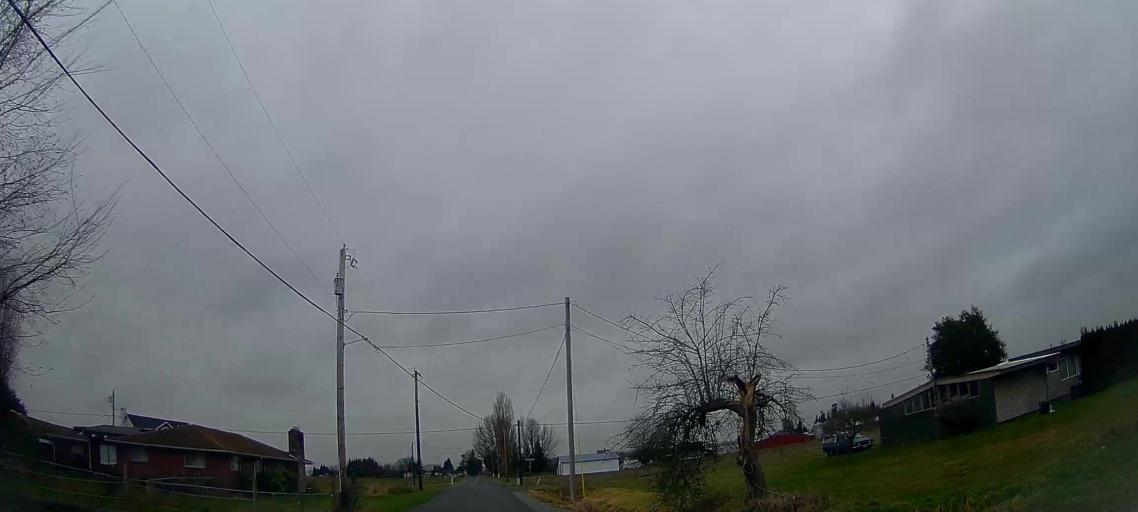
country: US
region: Washington
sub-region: Skagit County
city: Mount Vernon
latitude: 48.3704
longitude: -122.3232
